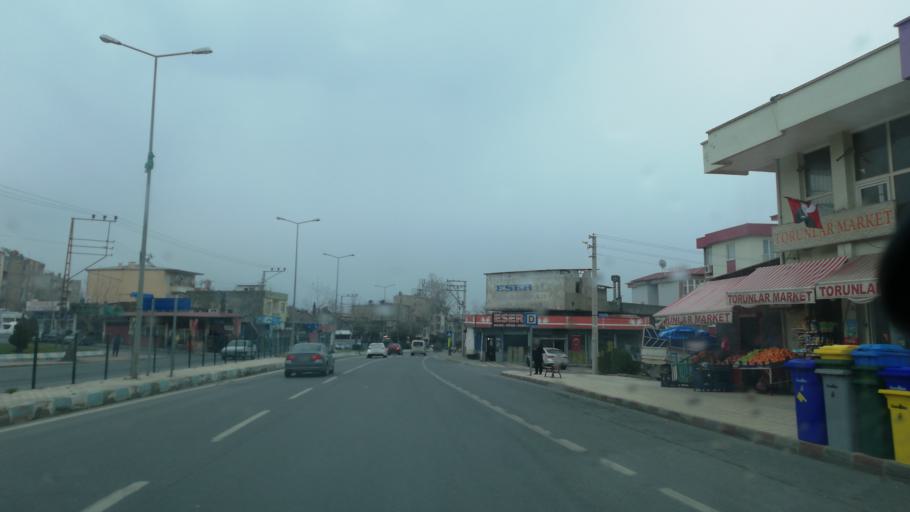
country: TR
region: Kahramanmaras
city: Kahramanmaras
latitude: 37.5702
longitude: 36.9449
